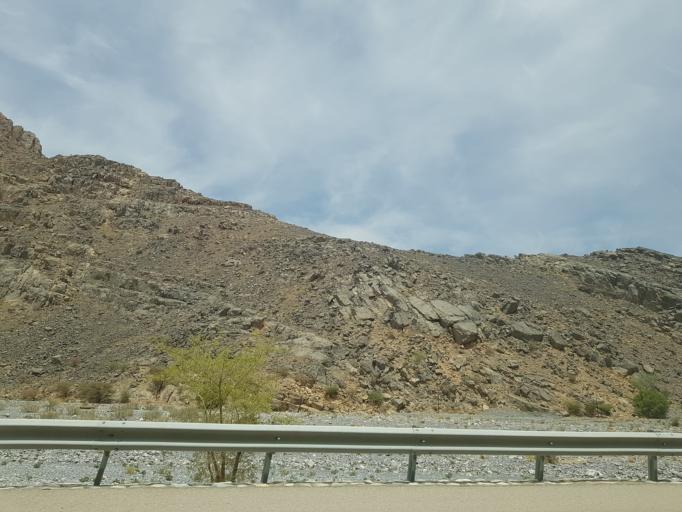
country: OM
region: Muhafazat ad Dakhiliyah
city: Izki
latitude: 22.9348
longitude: 57.6711
